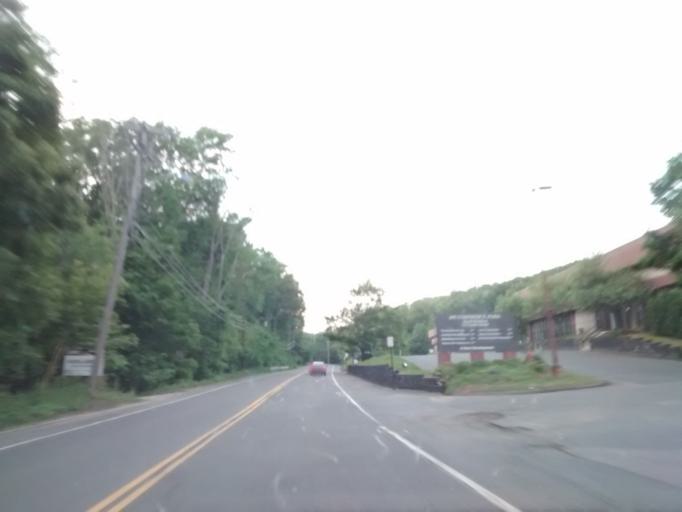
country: US
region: Massachusetts
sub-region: Worcester County
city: Milford
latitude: 42.1694
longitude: -71.5089
